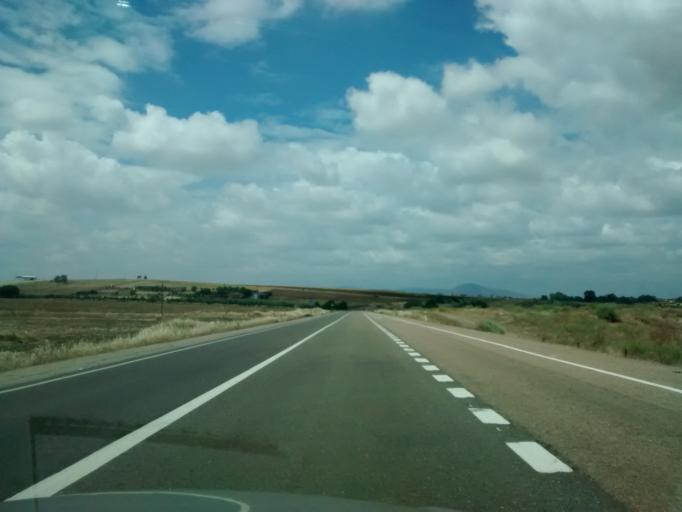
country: ES
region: Extremadura
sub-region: Provincia de Badajoz
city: Trujillanos
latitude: 38.9437
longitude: -6.2897
